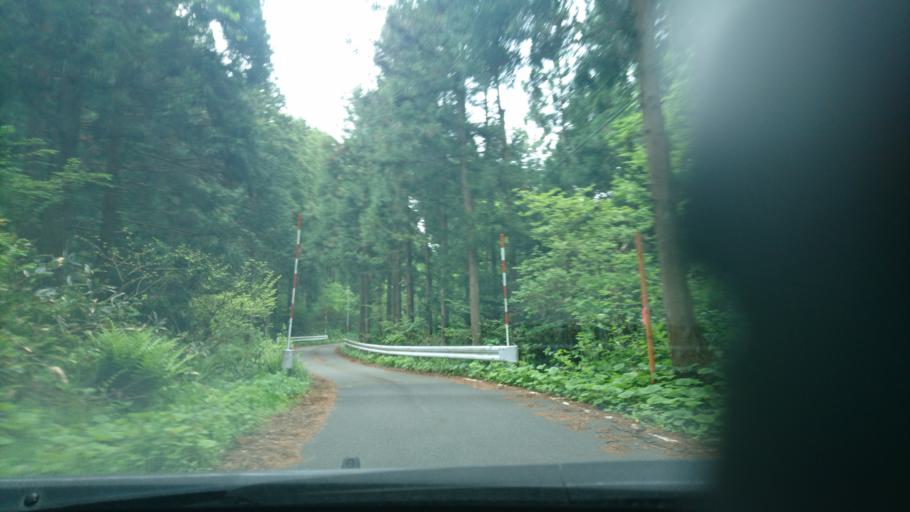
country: JP
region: Iwate
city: Ichinoseki
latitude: 38.9047
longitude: 140.9134
